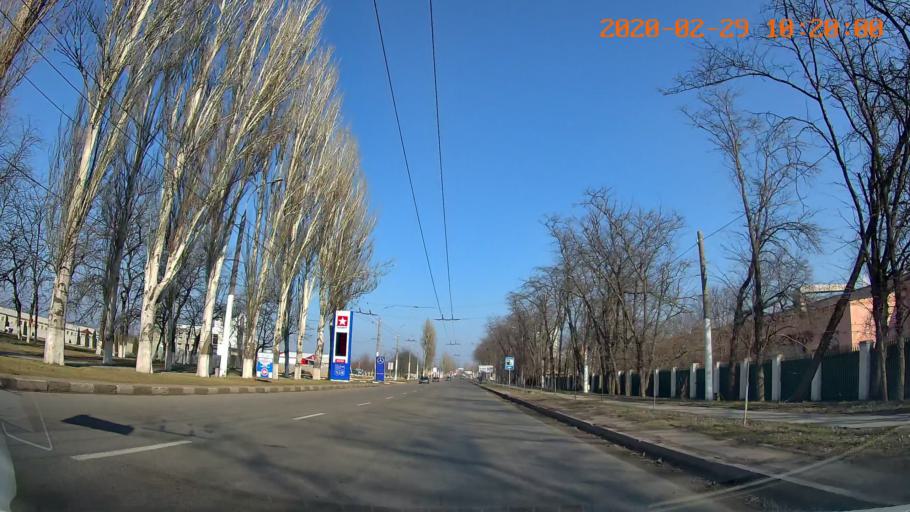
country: MD
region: Telenesti
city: Tiraspolul Nou
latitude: 46.8564
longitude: 29.6115
